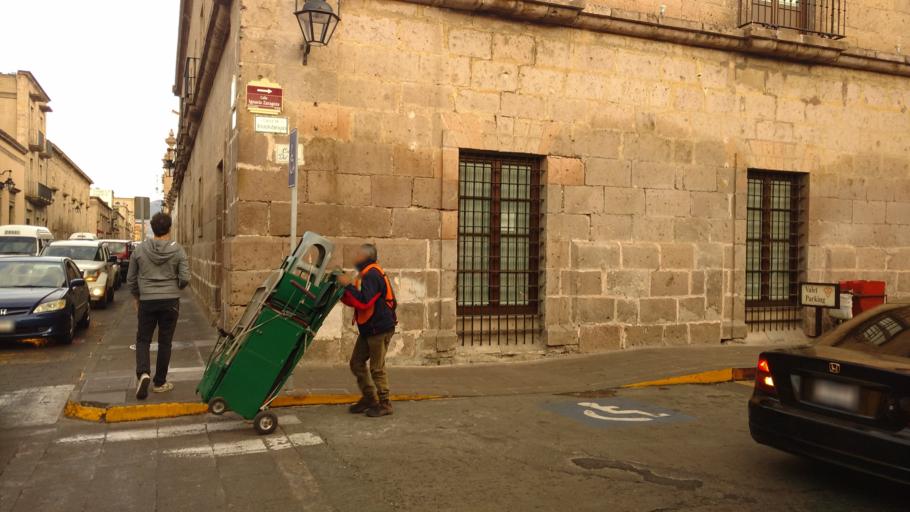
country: MX
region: Michoacan
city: Morelia
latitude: 19.7038
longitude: -101.1932
